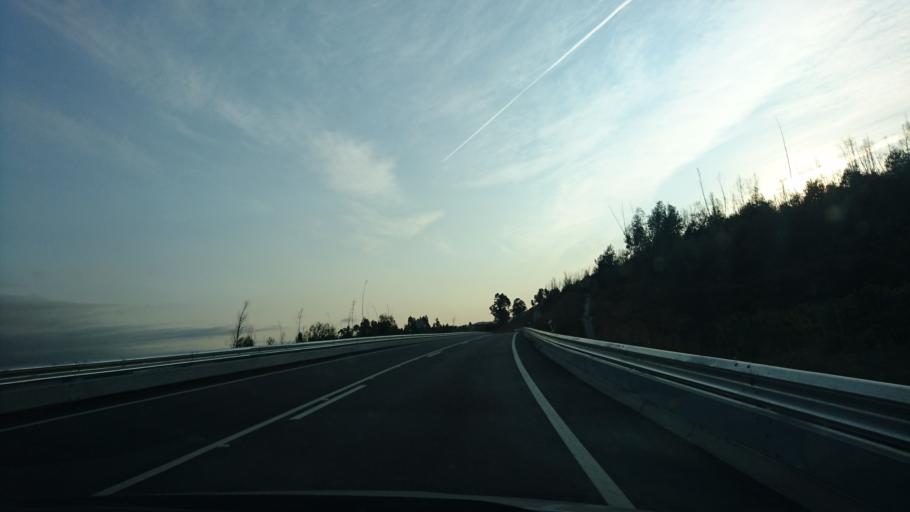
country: PT
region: Braga
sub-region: Celorico de Basto
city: Celorico de Basto
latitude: 41.4034
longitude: -7.9809
